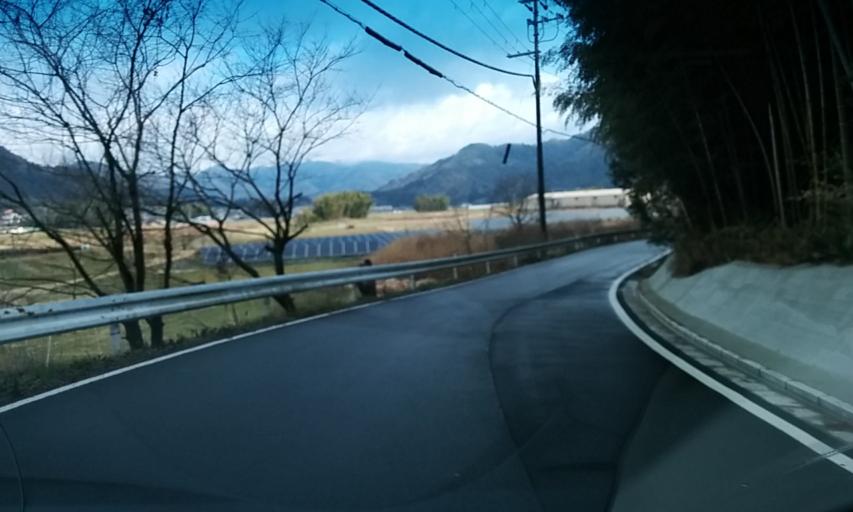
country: JP
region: Kyoto
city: Ayabe
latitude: 35.1783
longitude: 135.4100
